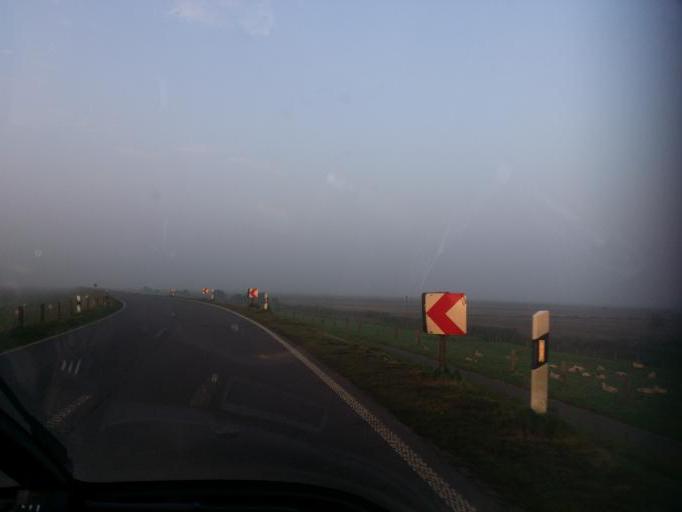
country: DE
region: Schleswig-Holstein
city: Wobbenbull
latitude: 54.5251
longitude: 8.9832
